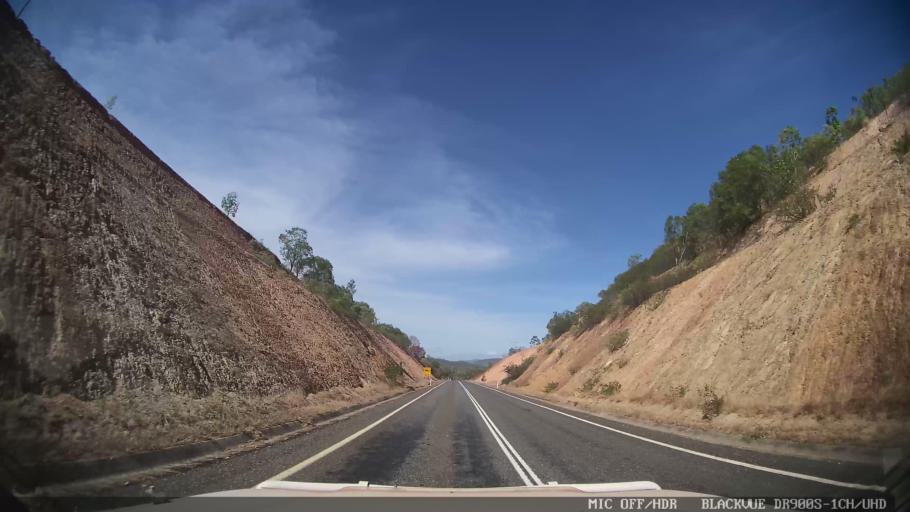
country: AU
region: Queensland
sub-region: Cook
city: Cooktown
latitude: -15.6965
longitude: 145.0380
